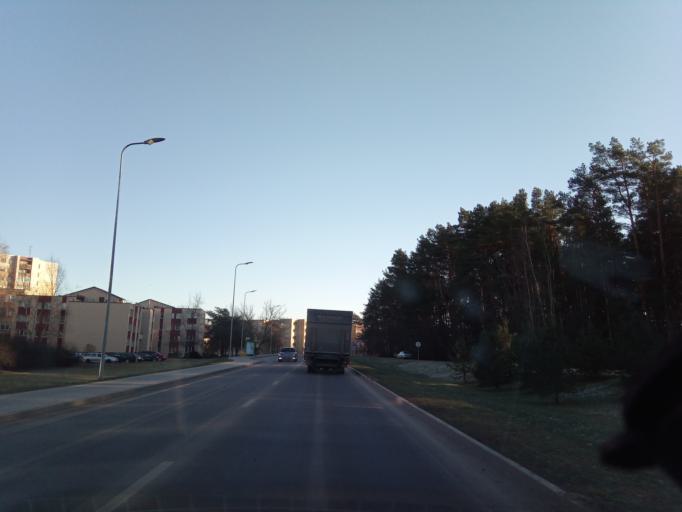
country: LT
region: Alytaus apskritis
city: Druskininkai
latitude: 54.0257
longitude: 23.9977
